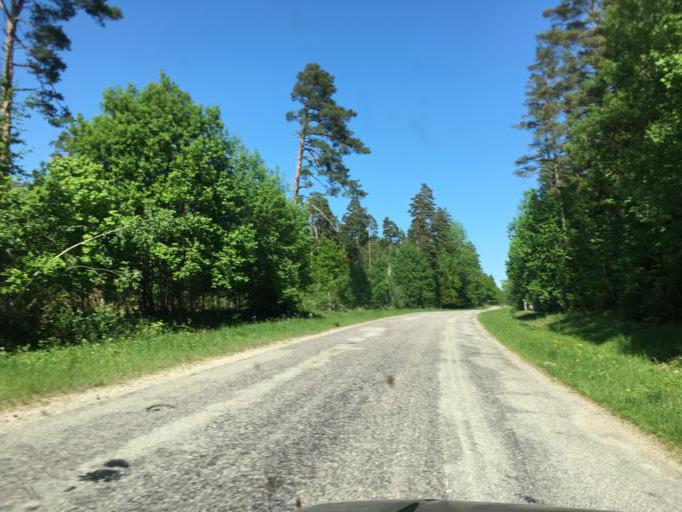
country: LV
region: Dundaga
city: Dundaga
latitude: 57.4764
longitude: 22.3245
